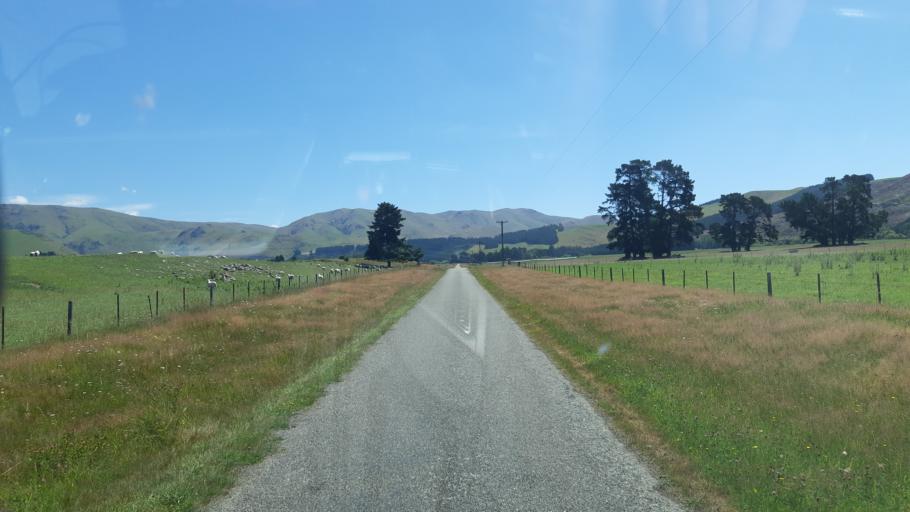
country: NZ
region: Canterbury
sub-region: Timaru District
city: Pleasant Point
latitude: -44.3366
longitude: 170.8970
